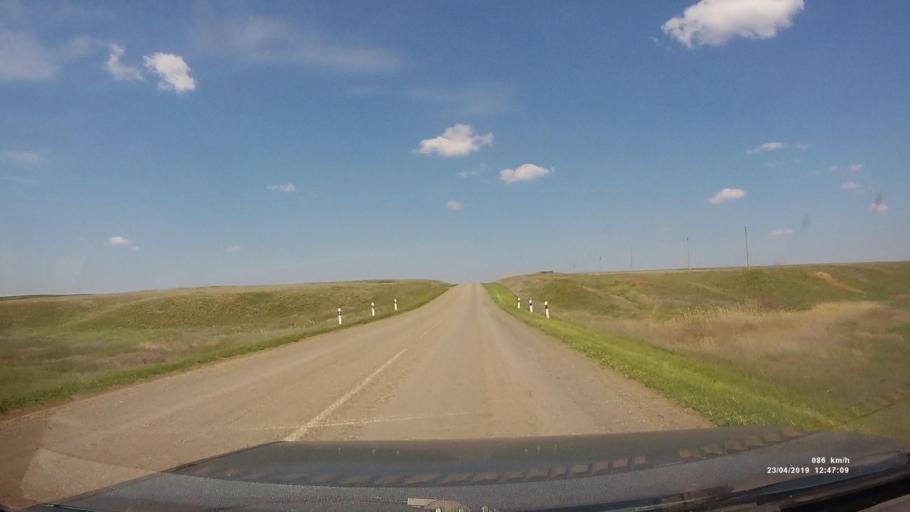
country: RU
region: Kalmykiya
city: Yashalta
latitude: 46.5087
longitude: 42.6385
